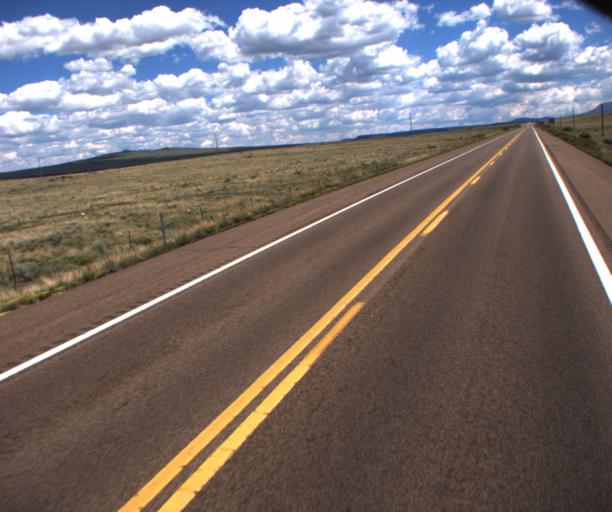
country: US
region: Arizona
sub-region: Apache County
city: Springerville
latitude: 34.1808
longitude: -109.3268
